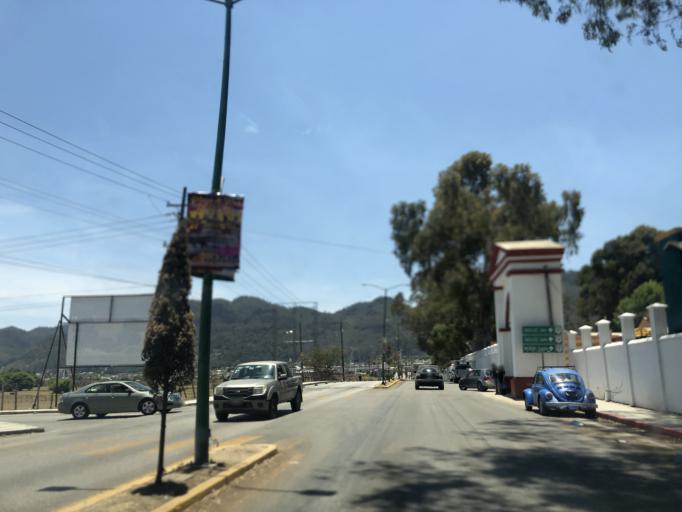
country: MX
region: Chiapas
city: San Cristobal de las Casas
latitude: 16.7258
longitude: -92.6515
